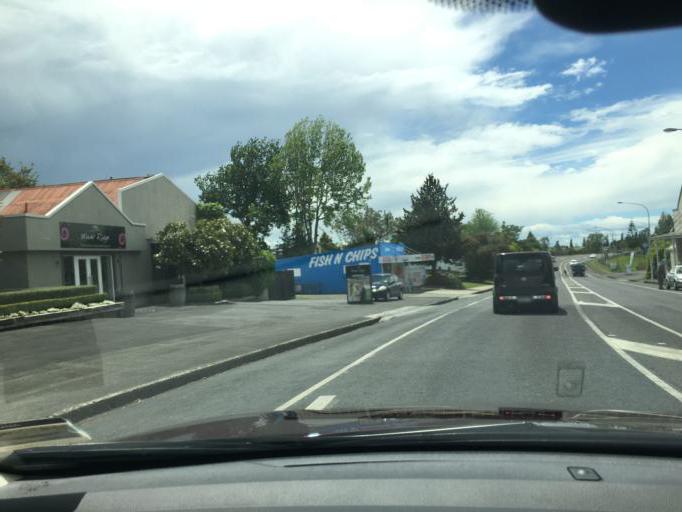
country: NZ
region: Waikato
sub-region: Hamilton City
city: Hamilton
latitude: -37.9188
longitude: 175.3068
